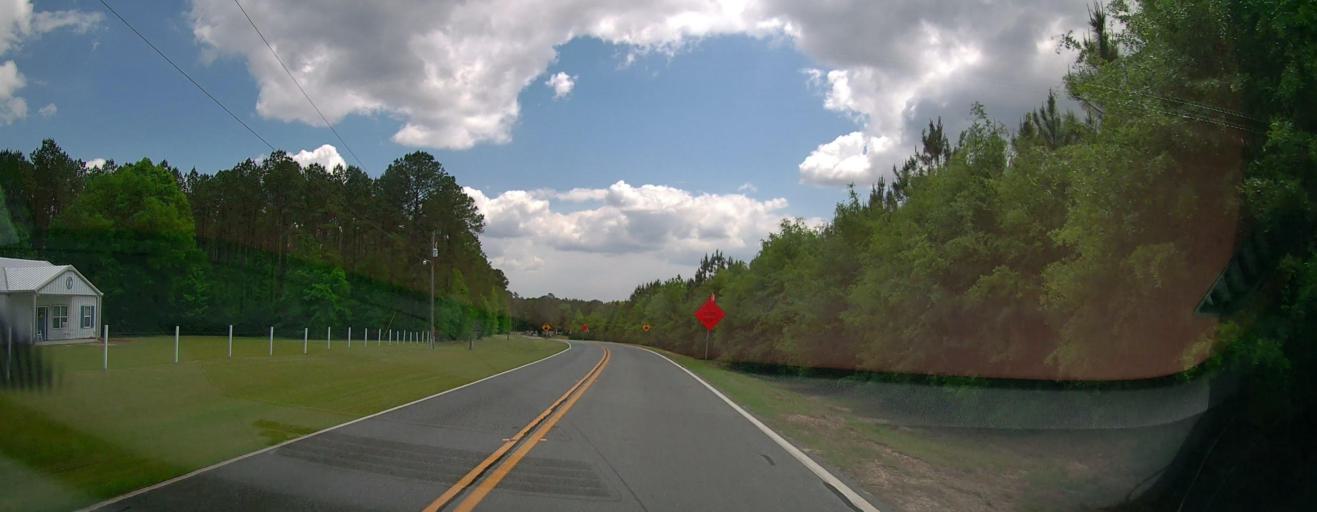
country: US
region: Georgia
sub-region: Treutlen County
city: Soperton
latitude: 32.4853
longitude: -82.6017
